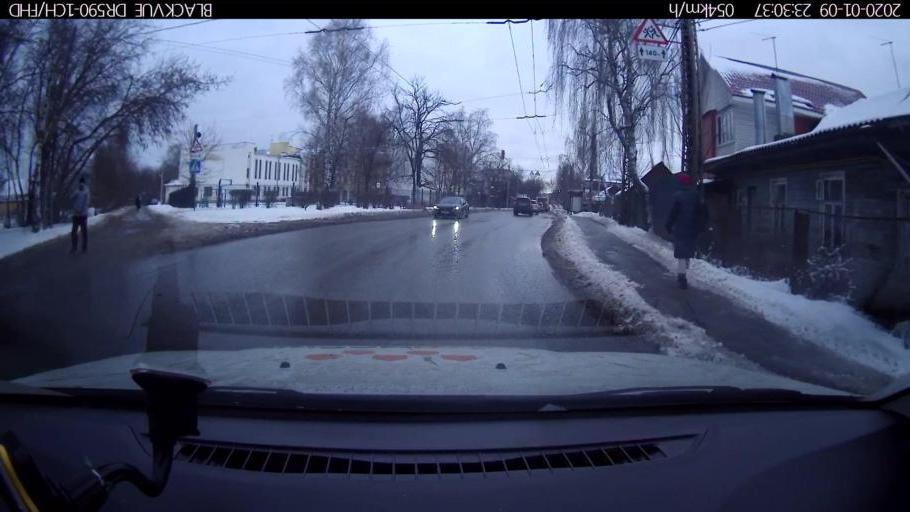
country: RU
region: Nizjnij Novgorod
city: Neklyudovo
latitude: 56.3626
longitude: 43.8439
